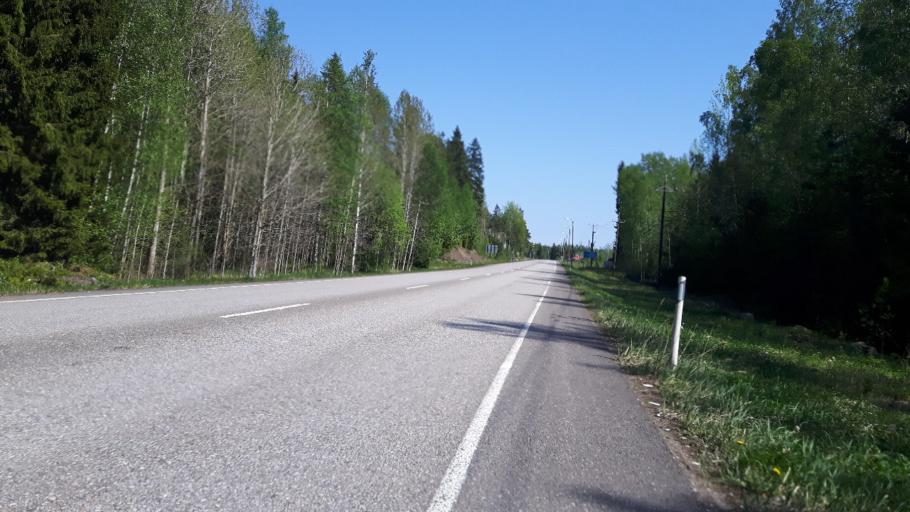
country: FI
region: Kymenlaakso
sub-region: Kotka-Hamina
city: Broby
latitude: 60.4890
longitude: 26.6556
